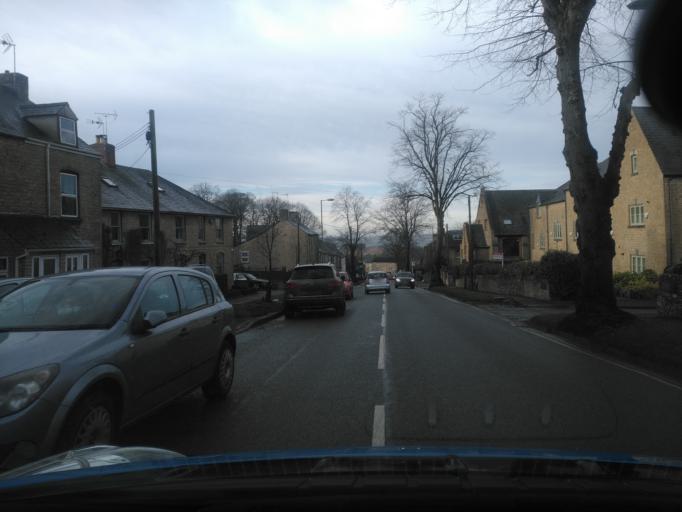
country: GB
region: England
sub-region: Oxfordshire
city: Chipping Norton
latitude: 51.9440
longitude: -1.5403
